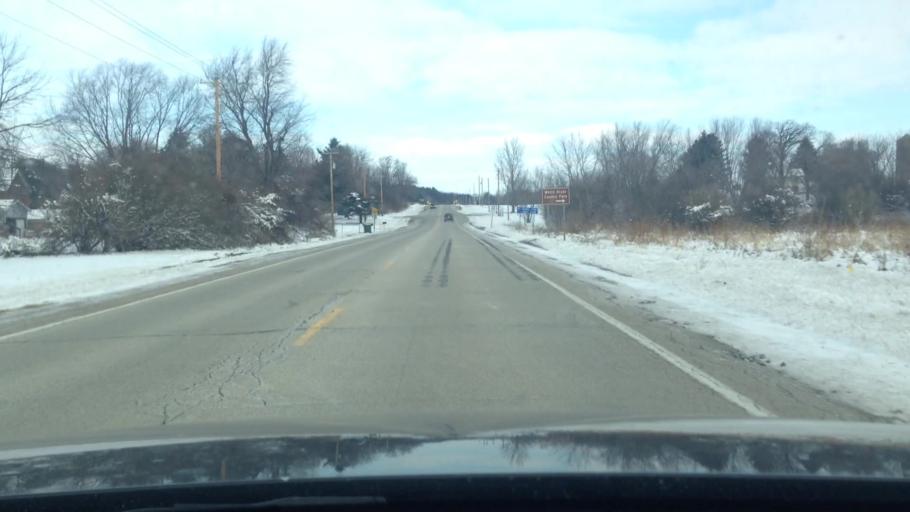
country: US
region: Wisconsin
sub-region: Walworth County
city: Lake Geneva
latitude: 42.6235
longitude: -88.4137
